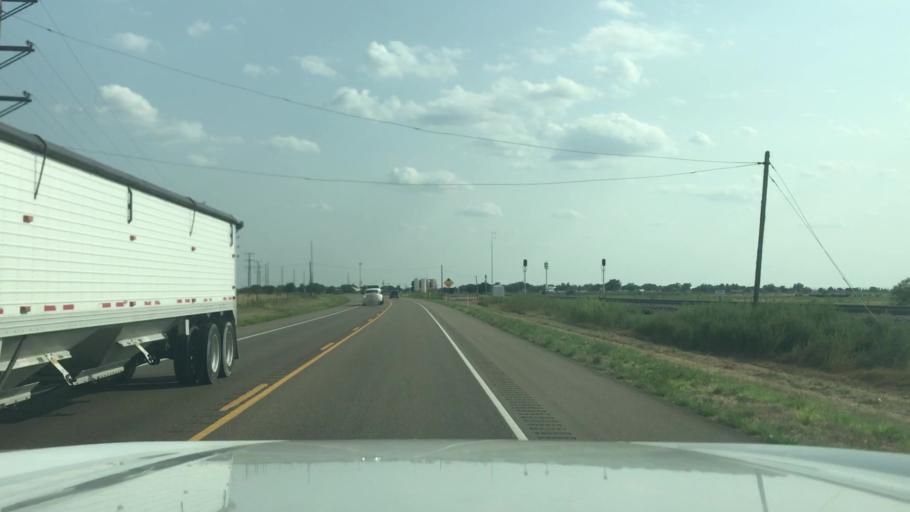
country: US
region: Texas
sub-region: Hartley County
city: Channing
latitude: 35.6966
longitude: -102.3277
